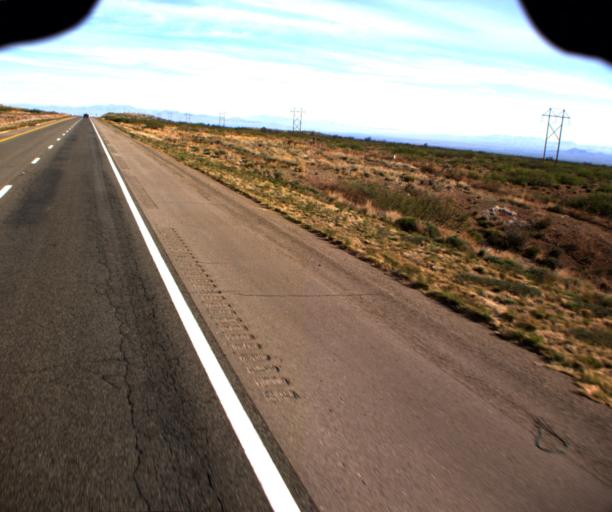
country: US
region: Arizona
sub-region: Graham County
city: Swift Trail Junction
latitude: 32.4988
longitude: -109.6736
